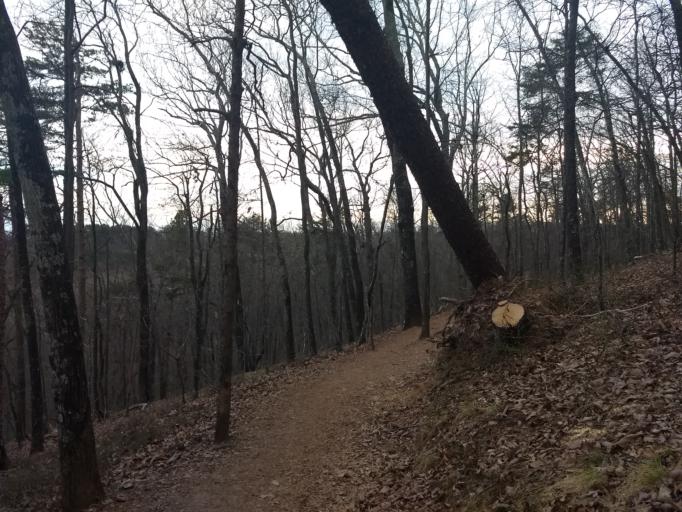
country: US
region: South Carolina
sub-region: Greenville County
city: Travelers Rest
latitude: 34.9448
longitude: -82.3901
